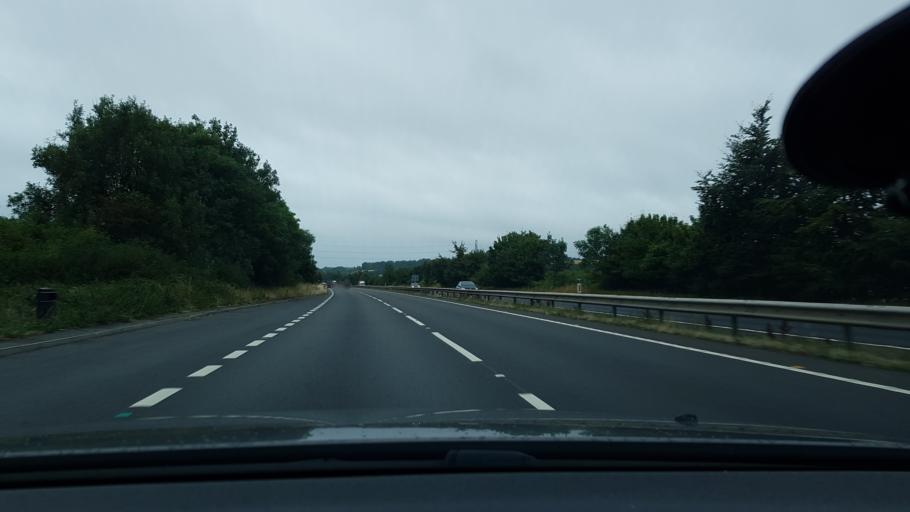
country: GB
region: England
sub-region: Hampshire
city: Highclere
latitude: 51.3027
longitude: -1.3363
